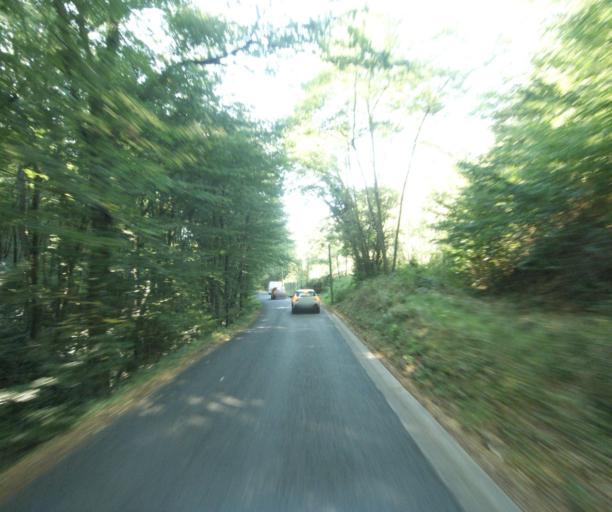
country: FR
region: Rhone-Alpes
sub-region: Departement du Rhone
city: Saint-Pierre-la-Palud
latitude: 45.7872
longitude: 4.6088
